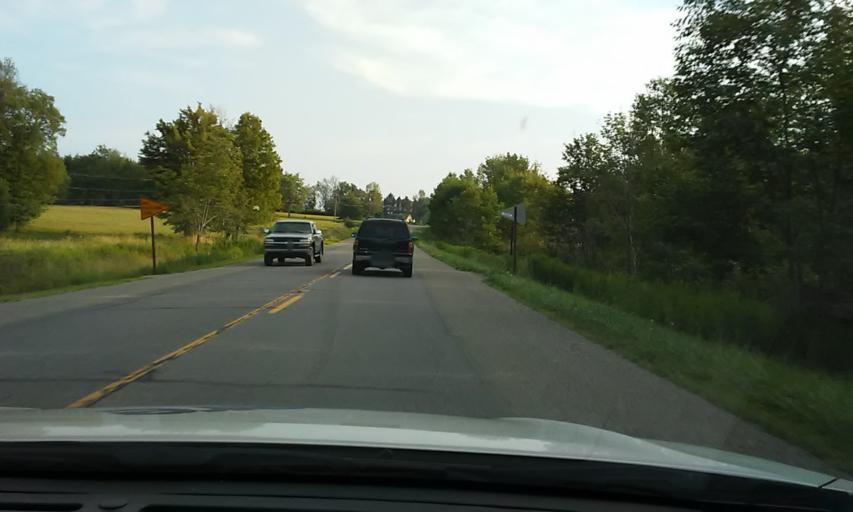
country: US
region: Pennsylvania
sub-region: McKean County
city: Kane
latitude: 41.6818
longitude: -78.7236
